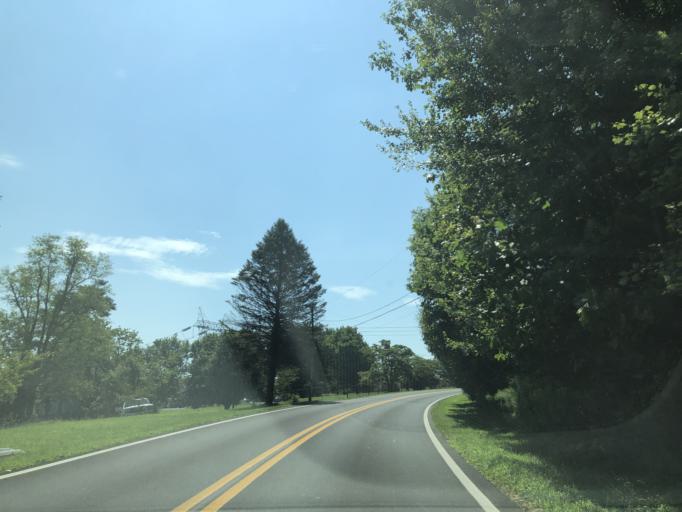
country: US
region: Maryland
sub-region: Carroll County
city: Eldersburg
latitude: 39.4521
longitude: -76.9711
